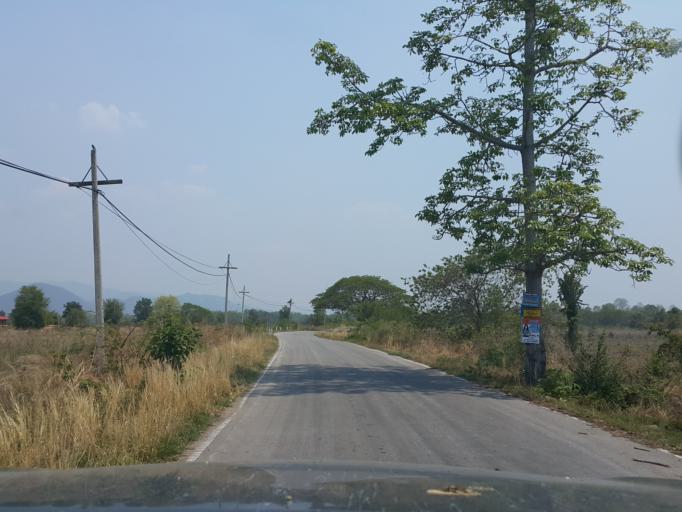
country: TH
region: Lampang
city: Mae Phrik
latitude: 17.5254
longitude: 99.1475
